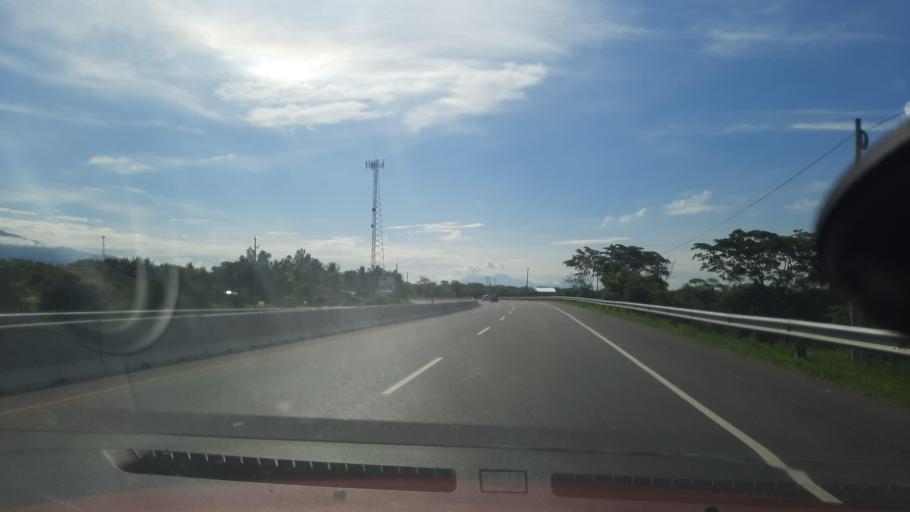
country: SV
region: La Paz
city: Santiago Nonualco
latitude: 13.4868
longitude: -88.9605
